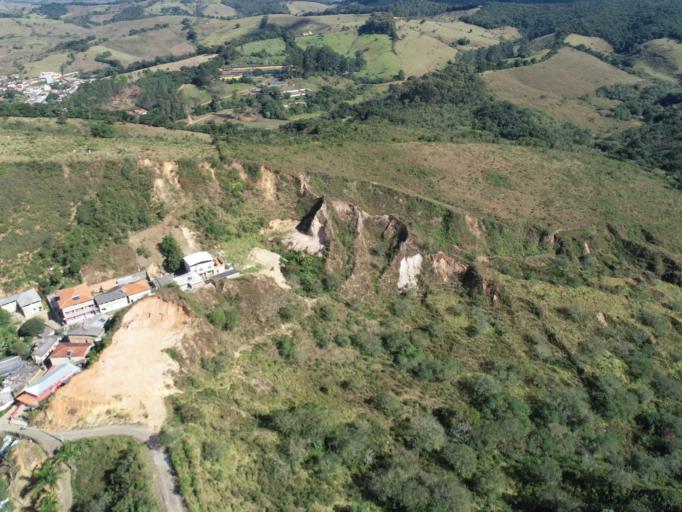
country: BR
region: Minas Gerais
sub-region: Tiradentes
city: Tiradentes
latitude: -21.0565
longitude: -44.0830
